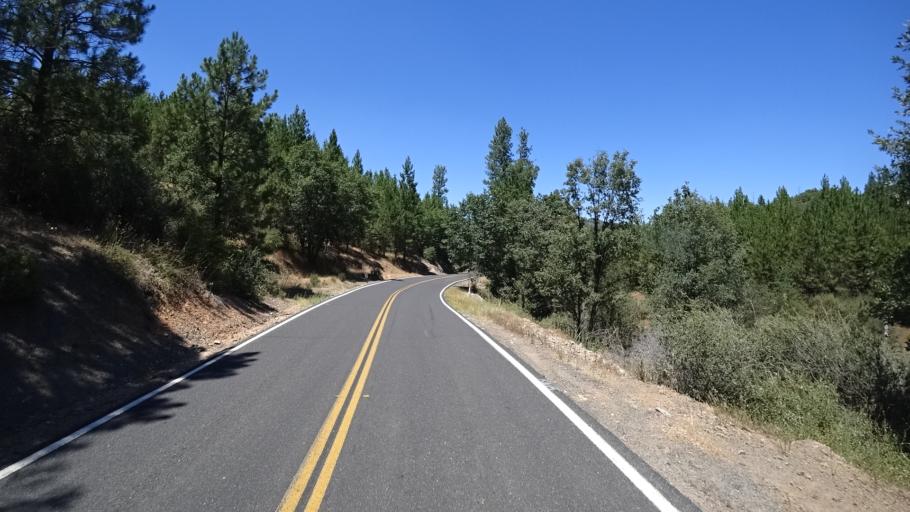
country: US
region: California
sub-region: Calaveras County
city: Mountain Ranch
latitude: 38.2902
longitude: -120.4932
